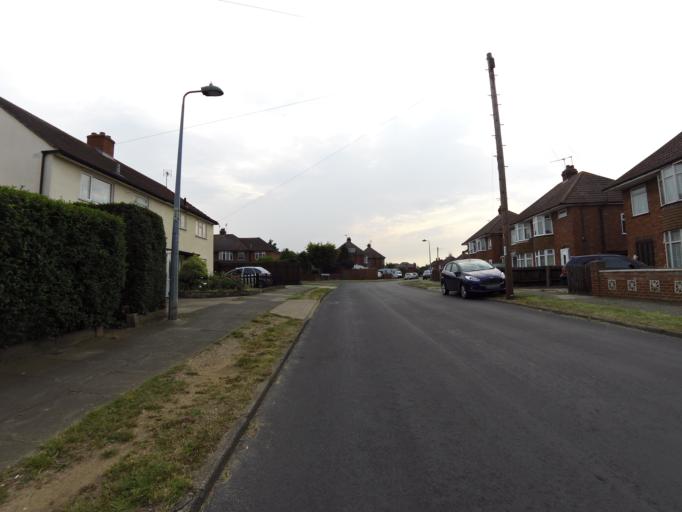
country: GB
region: England
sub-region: Suffolk
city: Ipswich
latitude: 52.0791
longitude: 1.1387
